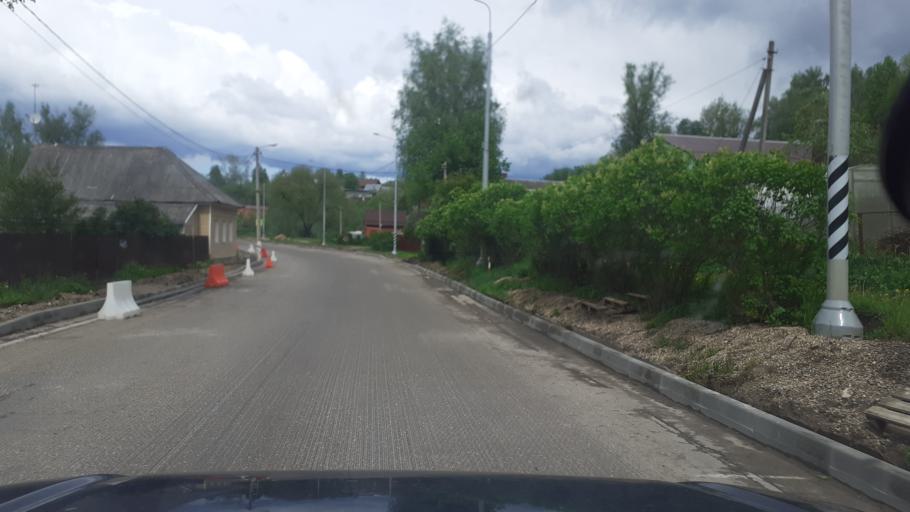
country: RU
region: Moskovskaya
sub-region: Volokolamskiy Rayon
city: Volokolamsk
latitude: 56.0393
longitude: 35.9551
